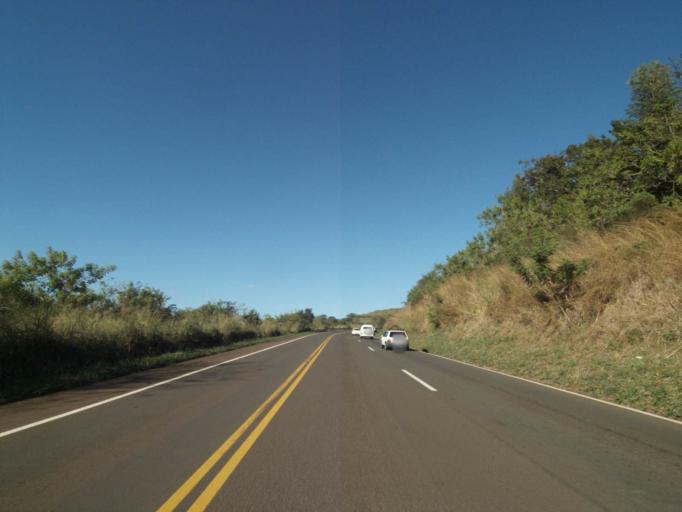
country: BR
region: Parana
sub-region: Londrina
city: Londrina
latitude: -23.6412
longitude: -51.1029
